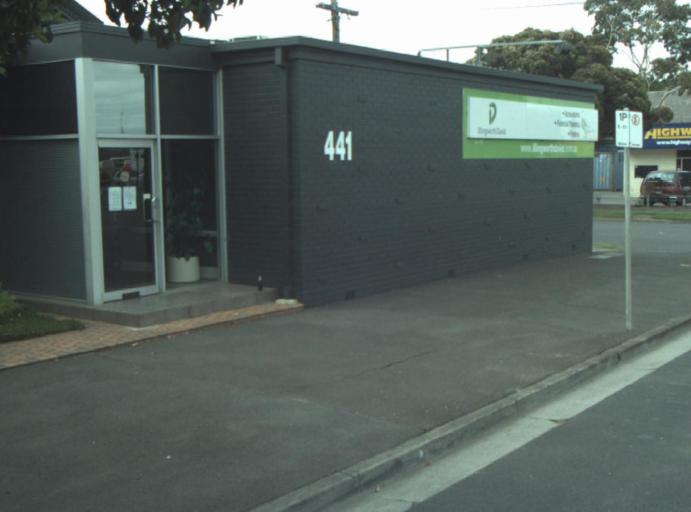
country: AU
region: Victoria
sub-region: Greater Geelong
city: Geelong
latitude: -38.1604
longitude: 144.3548
